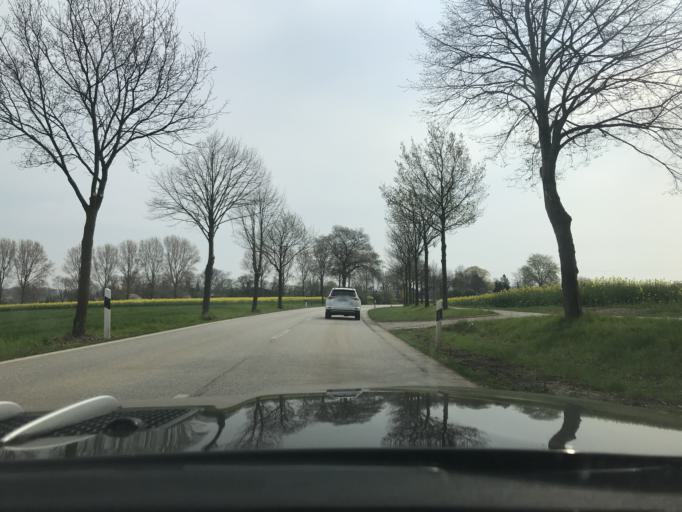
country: DE
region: Schleswig-Holstein
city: Heringsdorf
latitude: 54.2809
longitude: 11.0269
